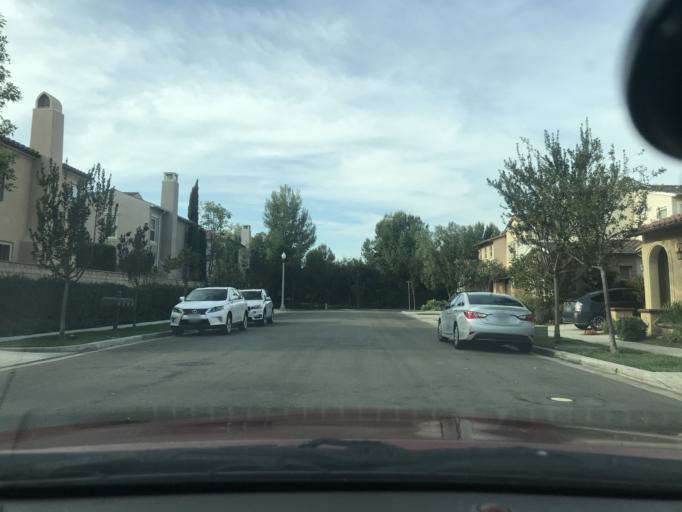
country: US
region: California
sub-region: Orange County
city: Irvine
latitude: 33.6986
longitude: -117.7575
